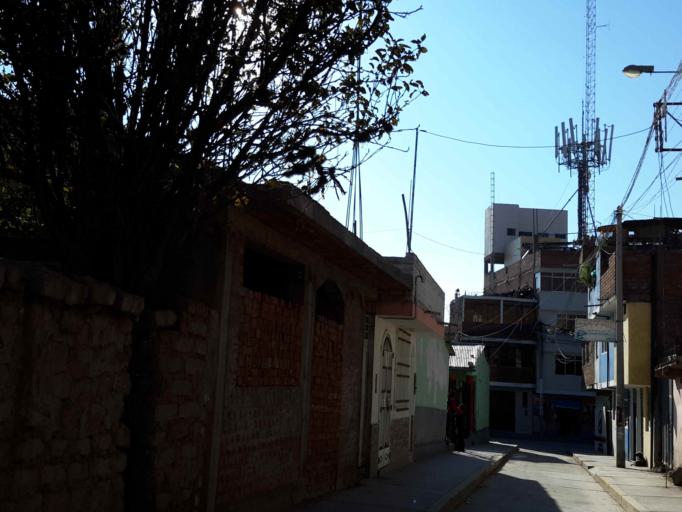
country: PE
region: Ayacucho
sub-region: Provincia de Huamanga
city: Ayacucho
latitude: -13.1537
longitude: -74.2220
